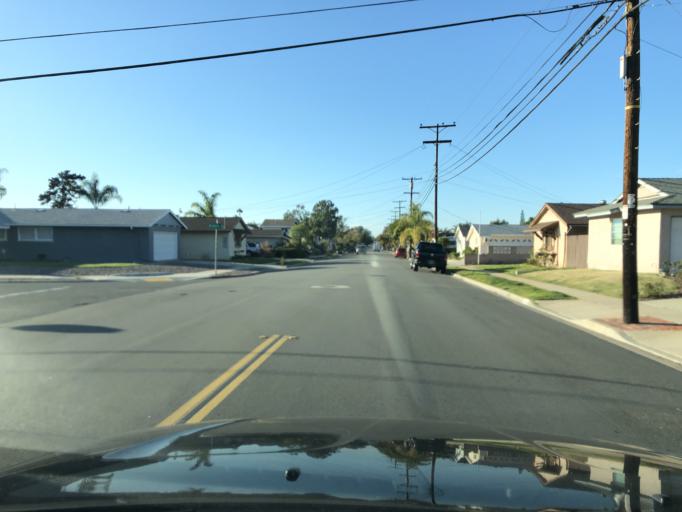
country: US
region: California
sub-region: San Diego County
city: La Jolla
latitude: 32.8212
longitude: -117.1876
